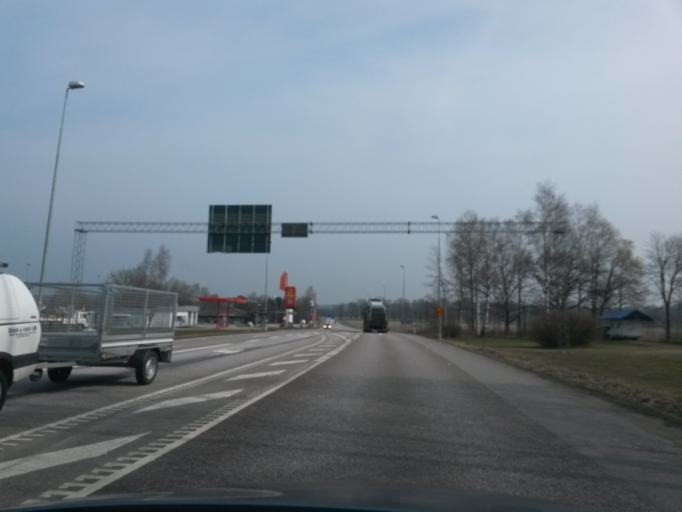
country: SE
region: Vaestra Goetaland
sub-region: Gullspangs Kommun
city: Hova
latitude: 58.8601
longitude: 14.2163
